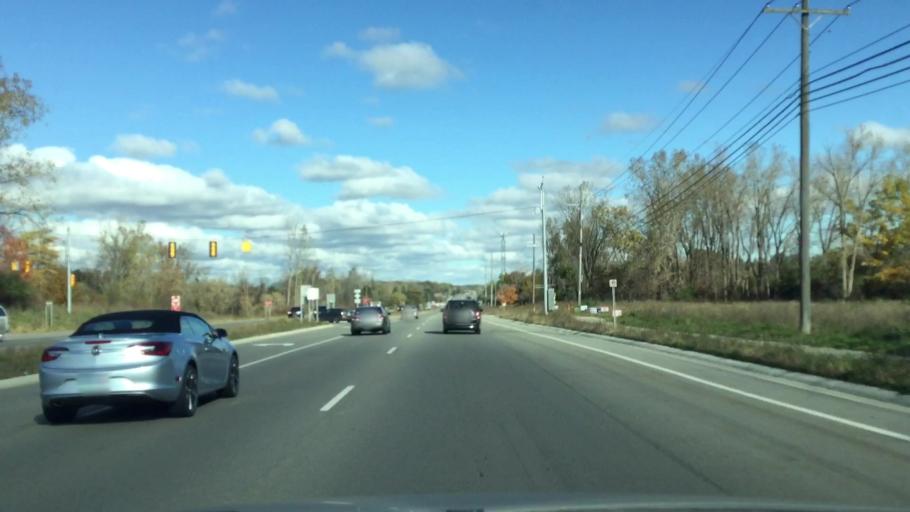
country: US
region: Michigan
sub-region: Oakland County
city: Auburn Hills
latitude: 42.7277
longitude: -83.2434
